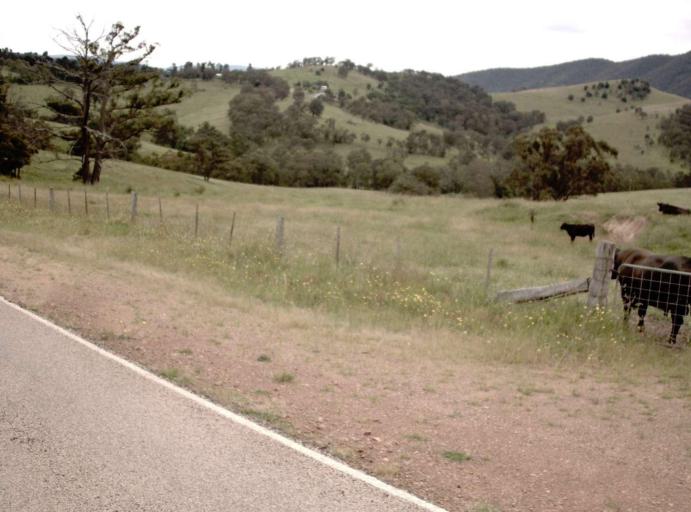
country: AU
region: Victoria
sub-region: East Gippsland
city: Bairnsdale
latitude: -37.5854
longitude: 147.1836
